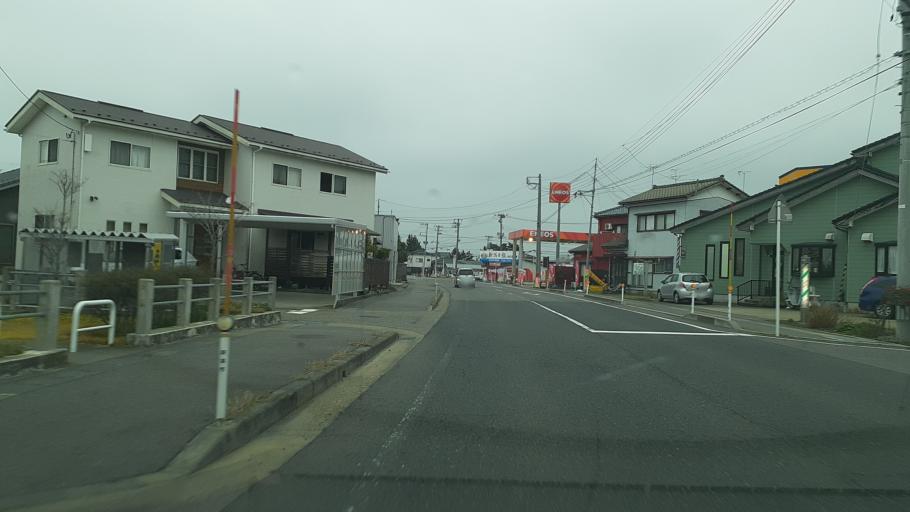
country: JP
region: Niigata
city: Niigata-shi
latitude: 37.8545
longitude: 139.0375
